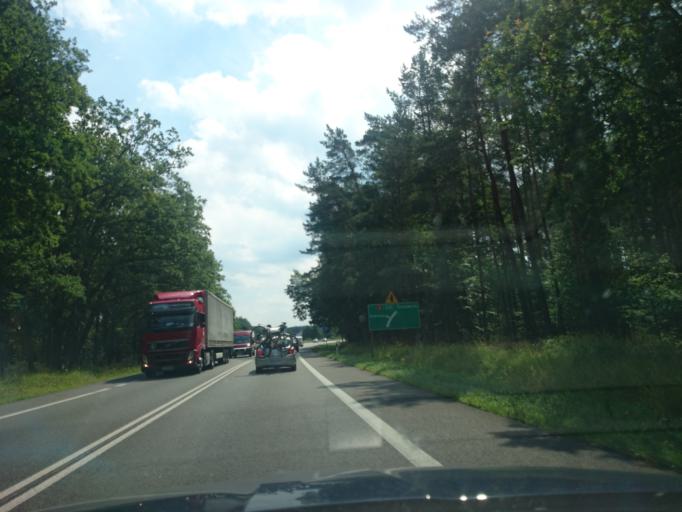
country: PL
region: West Pomeranian Voivodeship
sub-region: Powiat goleniowski
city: Przybiernow
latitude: 53.6840
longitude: 14.8041
